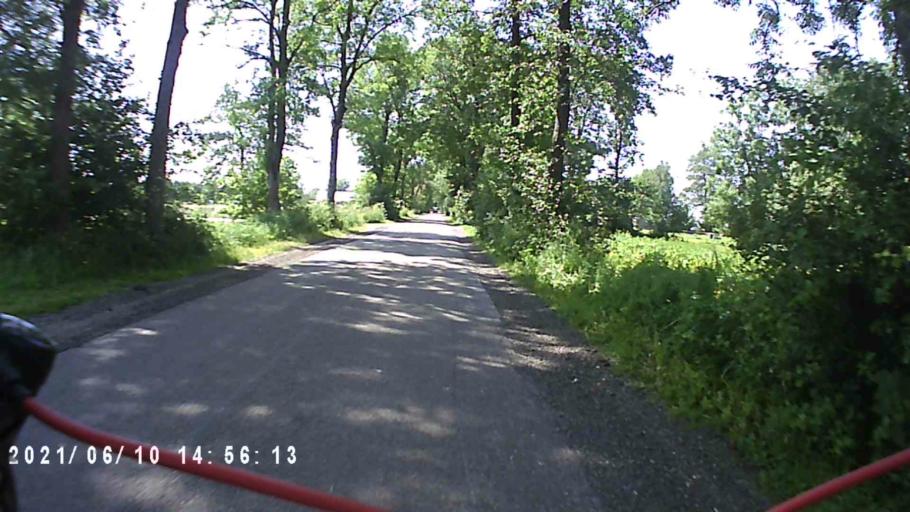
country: NL
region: Groningen
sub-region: Gemeente Grootegast
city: Grootegast
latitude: 53.2188
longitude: 6.2468
